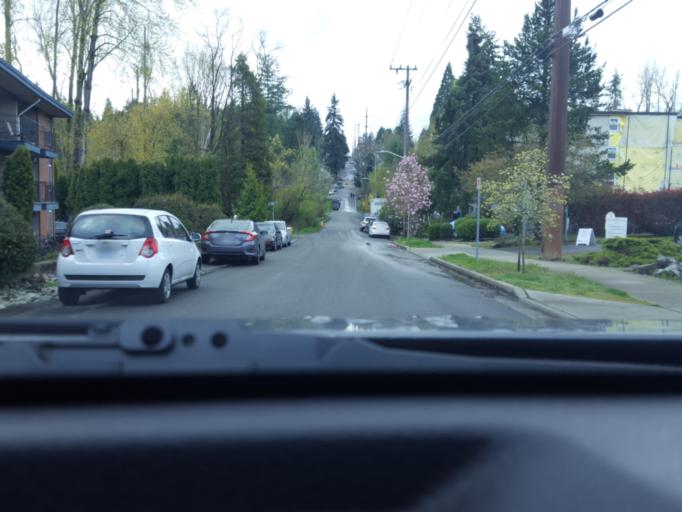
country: US
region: Washington
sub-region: King County
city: Shoreline
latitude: 47.7065
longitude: -122.3205
